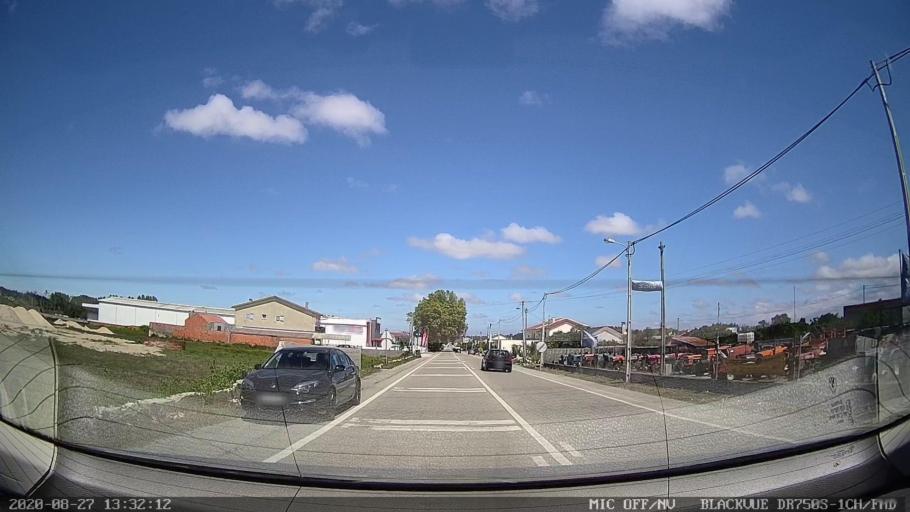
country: PT
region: Aveiro
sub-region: Vagos
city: Vagos
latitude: 40.4896
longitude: -8.6867
